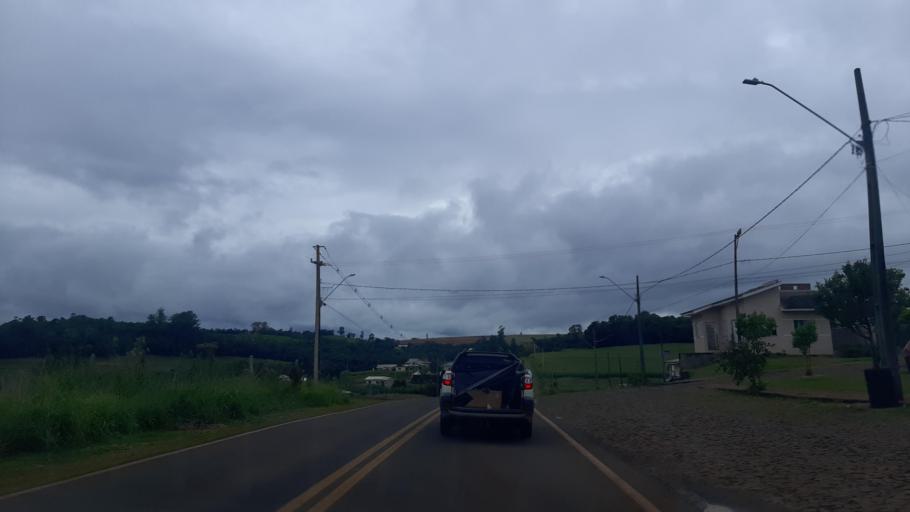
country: BR
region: Parana
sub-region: Ampere
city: Ampere
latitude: -25.9308
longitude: -53.4659
